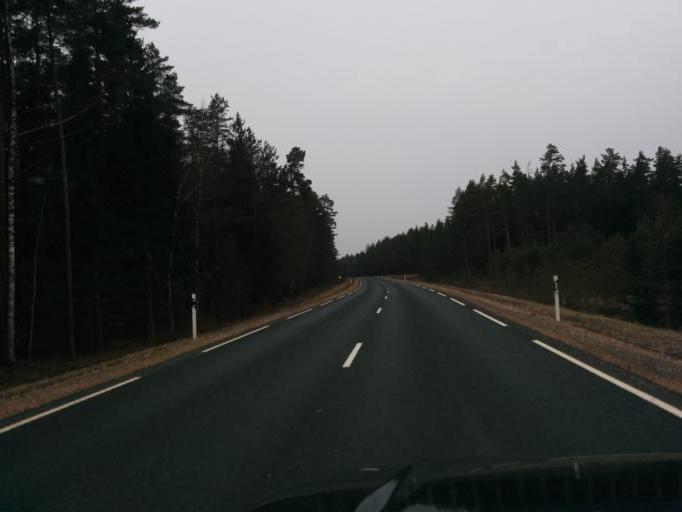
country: LV
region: Ogre
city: Ogre
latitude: 56.7975
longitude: 24.5934
